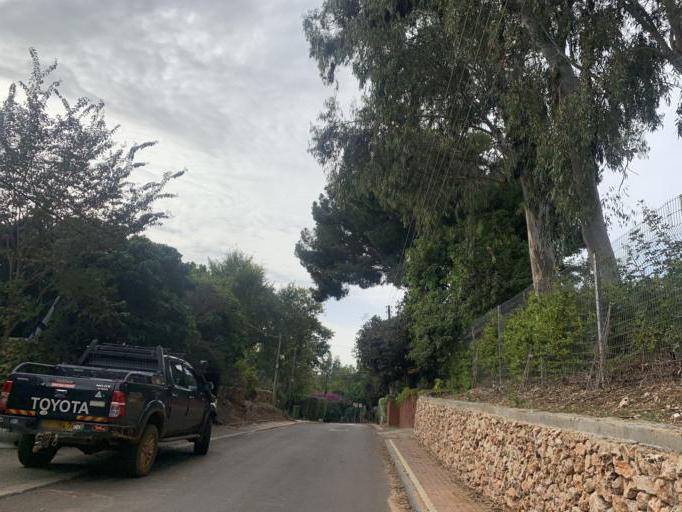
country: IL
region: Central District
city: Hod HaSharon
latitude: 32.1646
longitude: 34.8845
